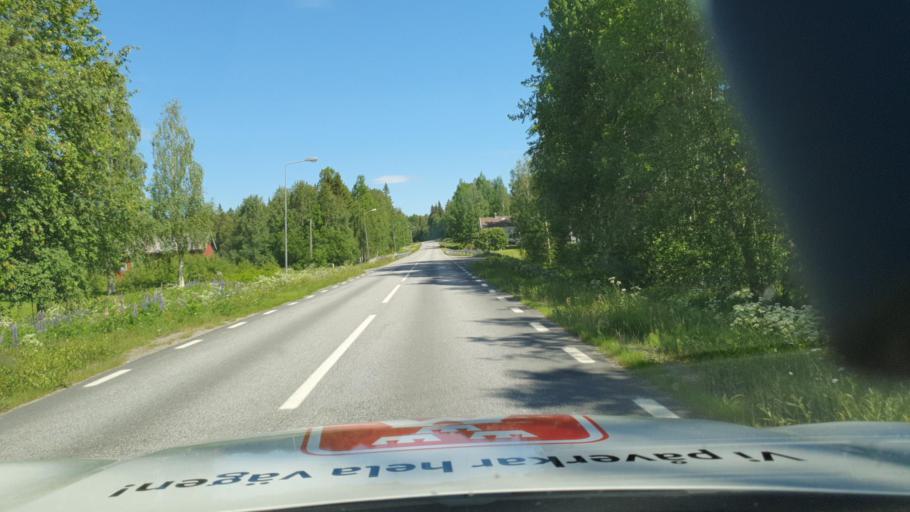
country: SE
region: Vaesterbotten
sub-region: Skelleftea Kommun
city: Boliden
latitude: 64.8443
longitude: 20.3704
